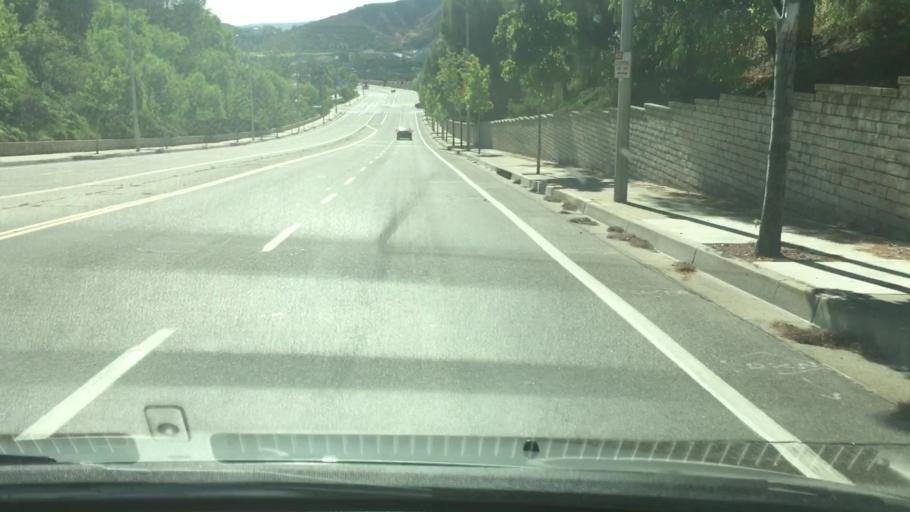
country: US
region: California
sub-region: Los Angeles County
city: Santa Clarita
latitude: 34.4597
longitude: -118.5143
